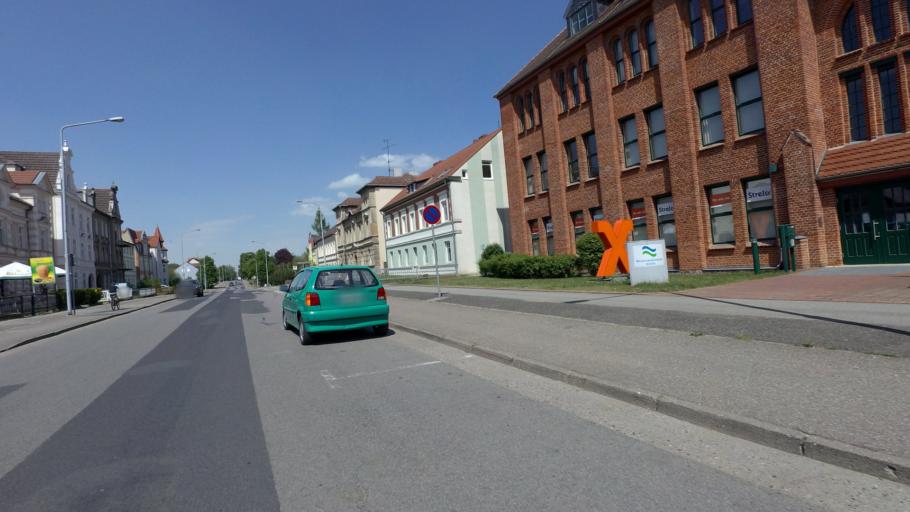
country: DE
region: Mecklenburg-Vorpommern
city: Neustrelitz
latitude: 53.3354
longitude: 13.0903
